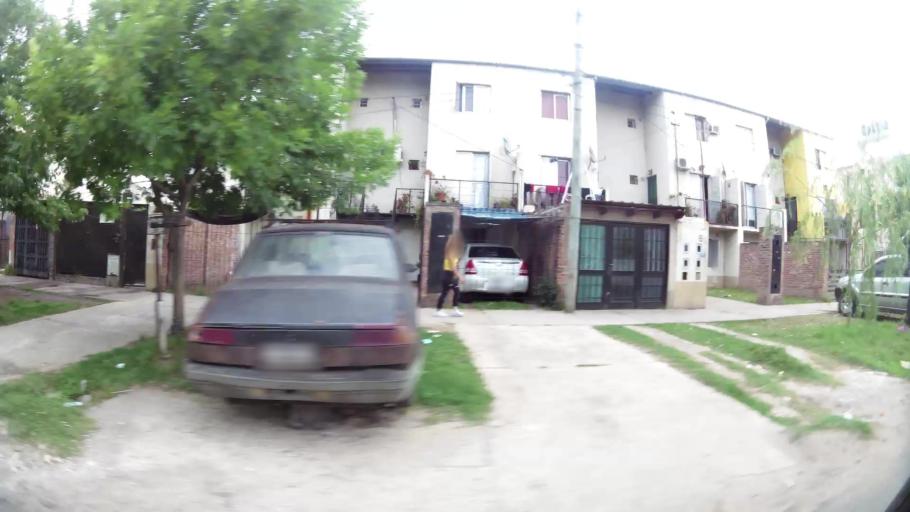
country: AR
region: Santa Fe
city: Gobernador Galvez
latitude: -33.0012
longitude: -60.6830
